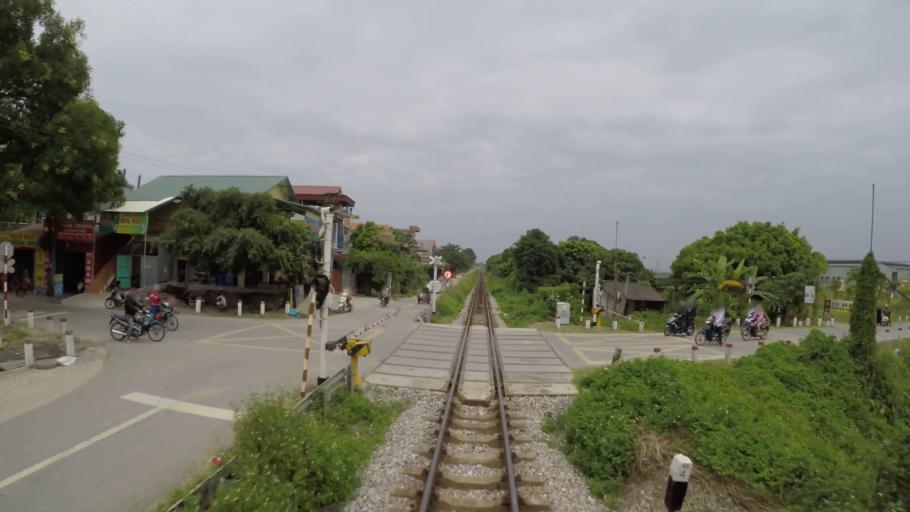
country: VN
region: Hai Duong
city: Lai Cach
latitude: 20.9517
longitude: 106.2349
